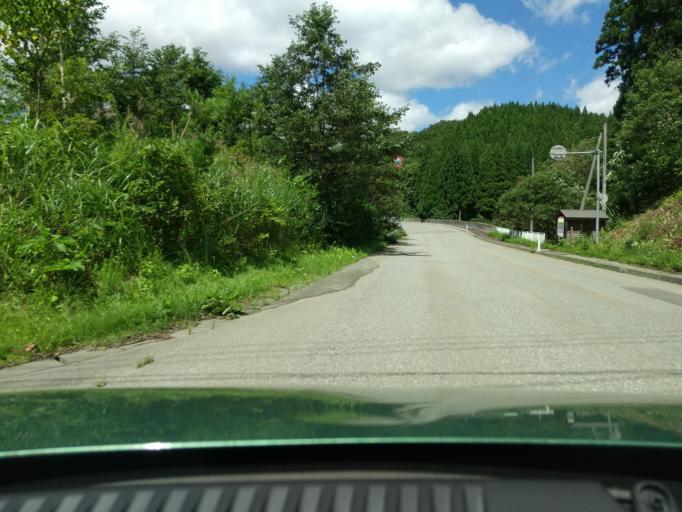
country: JP
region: Iwate
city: Shizukuishi
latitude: 39.7730
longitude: 140.7635
